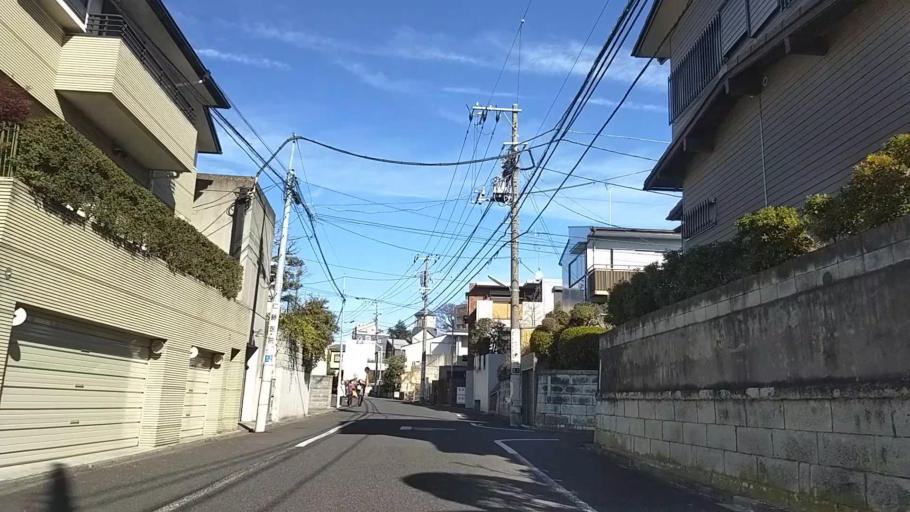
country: JP
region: Tokyo
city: Chofugaoka
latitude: 35.6206
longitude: 139.6269
